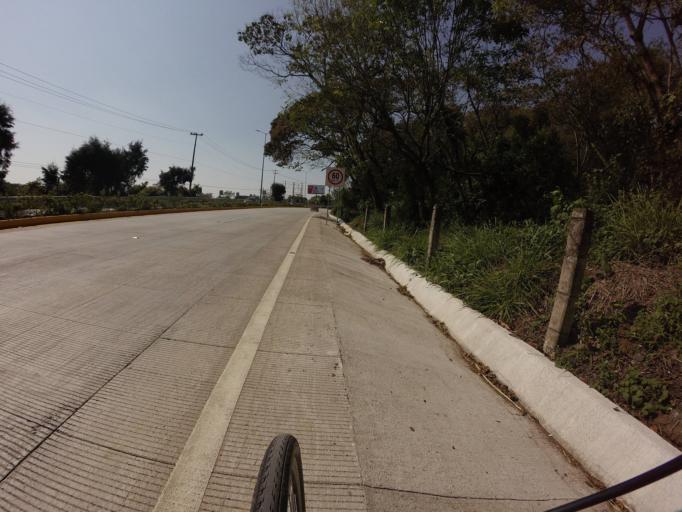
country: MX
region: Veracruz
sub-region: Xalapa
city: Xalapa de Enriquez
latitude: 19.4917
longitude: -96.9370
